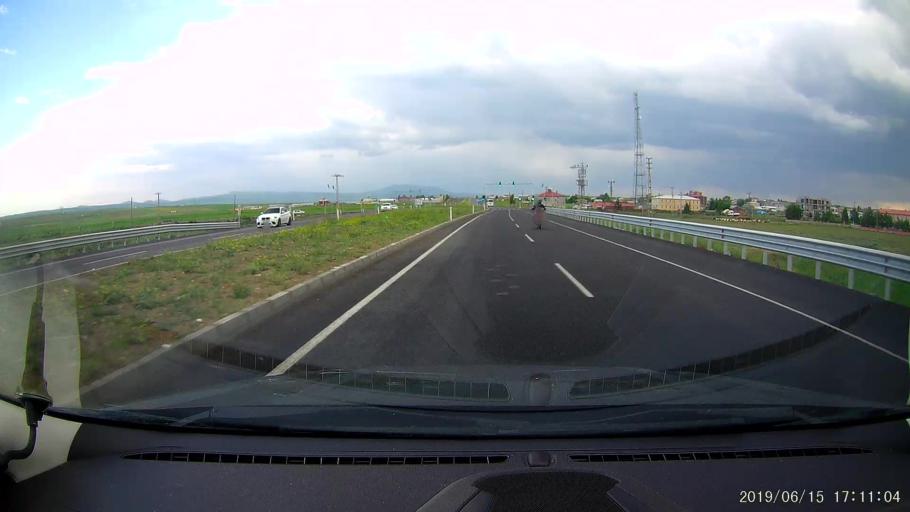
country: TR
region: Kars
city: Kars
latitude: 40.6150
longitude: 43.1334
